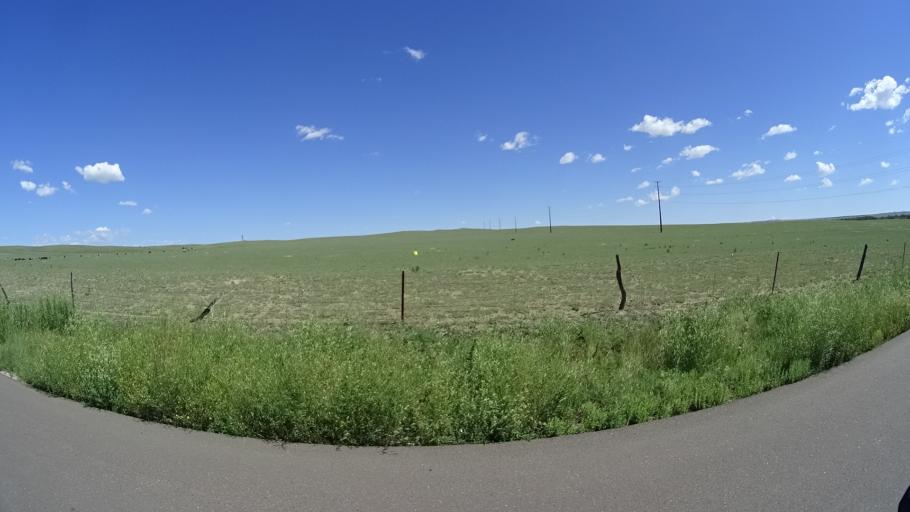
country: US
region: Colorado
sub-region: El Paso County
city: Security-Widefield
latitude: 38.7809
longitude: -104.6663
